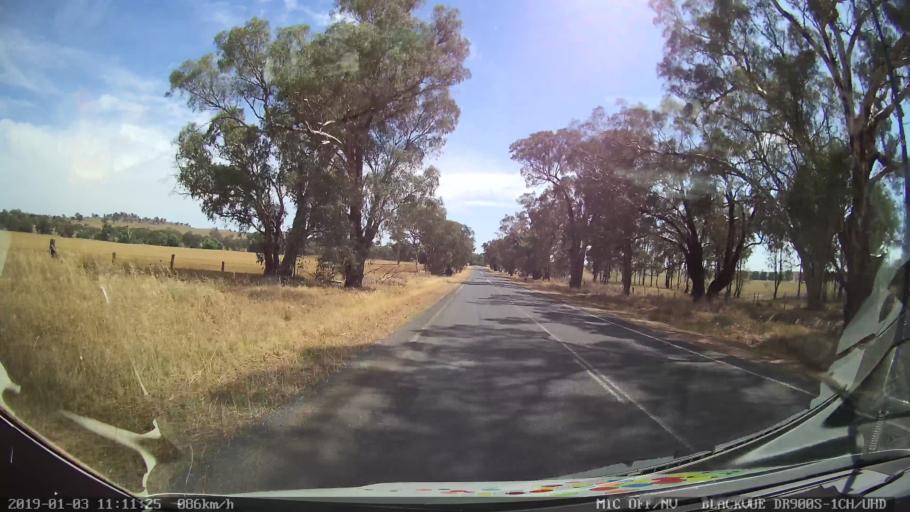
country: AU
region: New South Wales
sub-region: Young
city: Young
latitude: -34.2149
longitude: 148.2599
